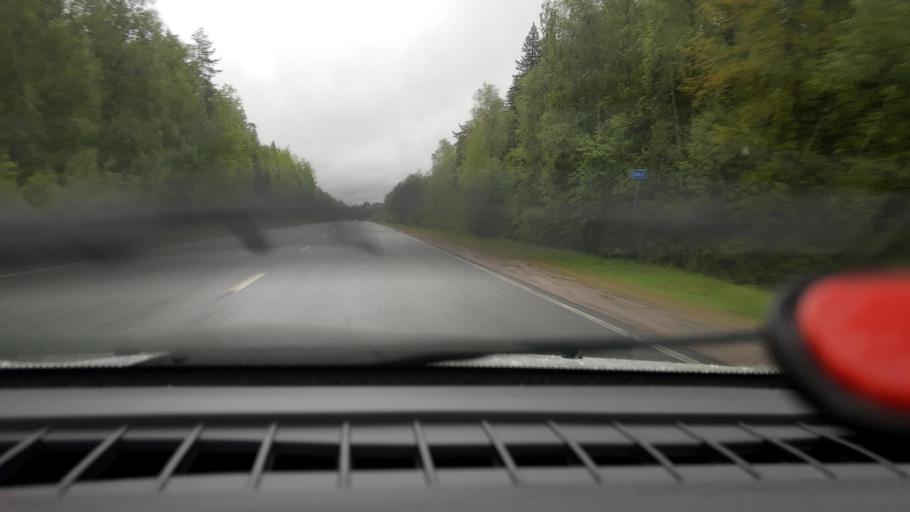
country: RU
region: Nizjnij Novgorod
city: Semenov
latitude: 56.8197
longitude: 44.5289
